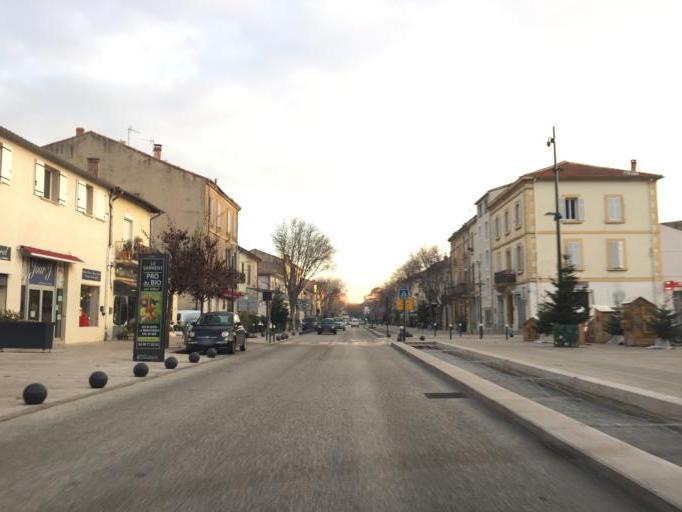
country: FR
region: Provence-Alpes-Cote d'Azur
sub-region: Departement du Vaucluse
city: Cavaillon
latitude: 43.8389
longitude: 5.0382
